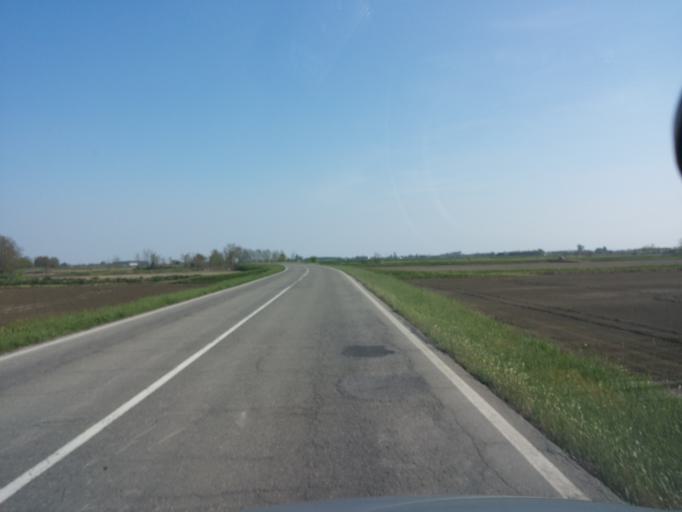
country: IT
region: Lombardy
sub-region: Provincia di Pavia
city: Langosco
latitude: 45.2026
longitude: 8.5790
